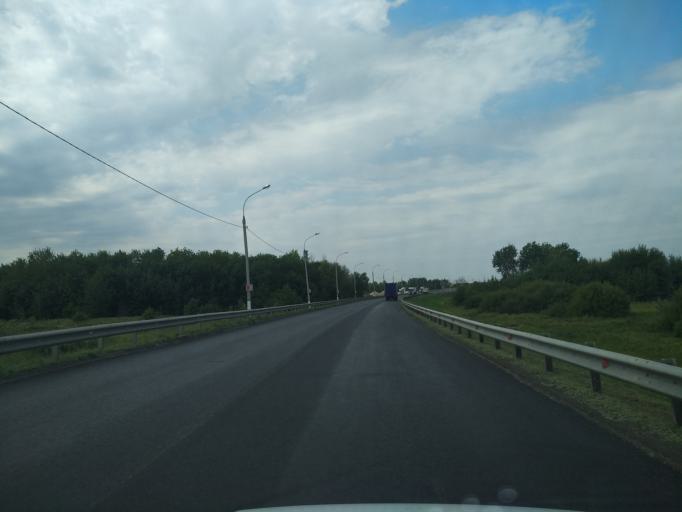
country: RU
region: Voronezj
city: Pereleshino
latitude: 51.7672
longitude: 40.1342
